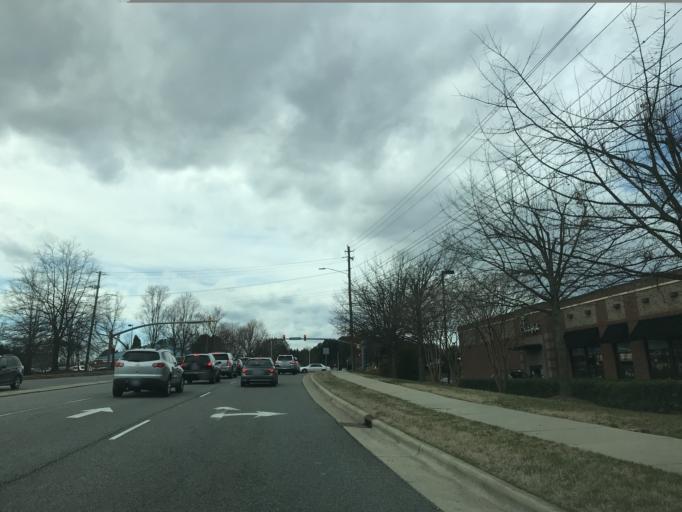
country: US
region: North Carolina
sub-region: Wake County
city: Morrisville
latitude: 35.7905
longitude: -78.8496
